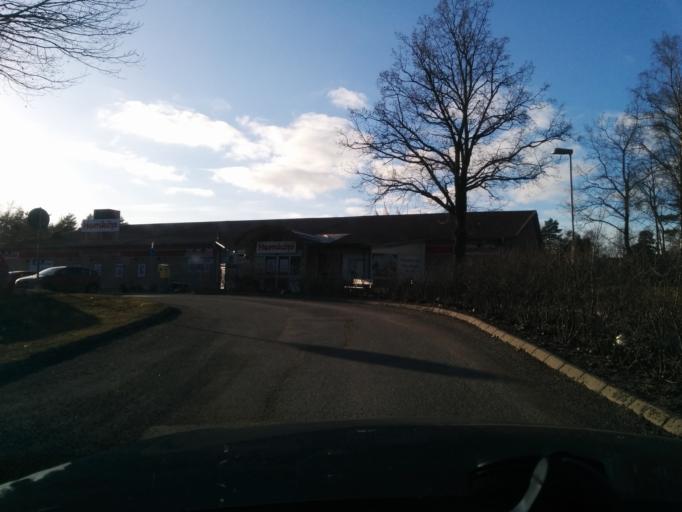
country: SE
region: Vaestmanland
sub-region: Vasteras
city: Vasteras
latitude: 59.6268
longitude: 16.5819
